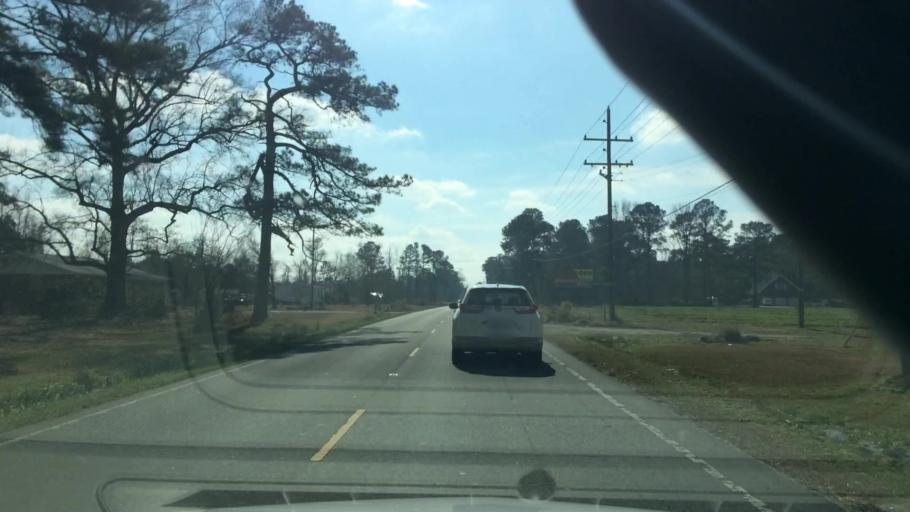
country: US
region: North Carolina
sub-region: Duplin County
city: Beulaville
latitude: 34.9007
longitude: -77.7803
